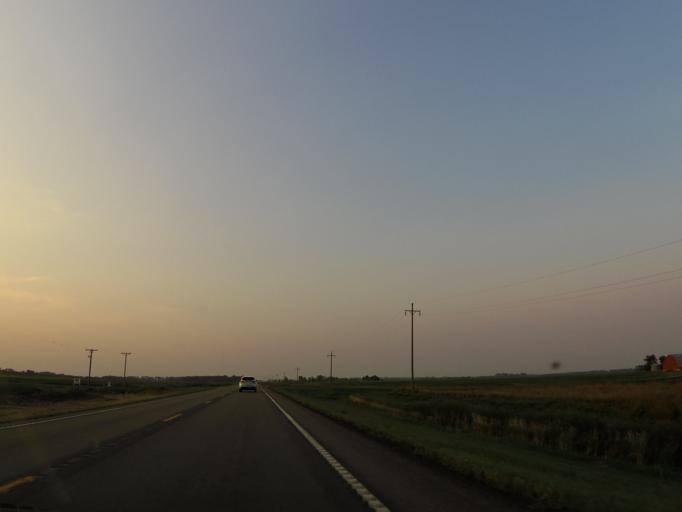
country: US
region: North Dakota
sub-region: Grand Forks County
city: Larimore
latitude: 48.1212
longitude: -97.6225
